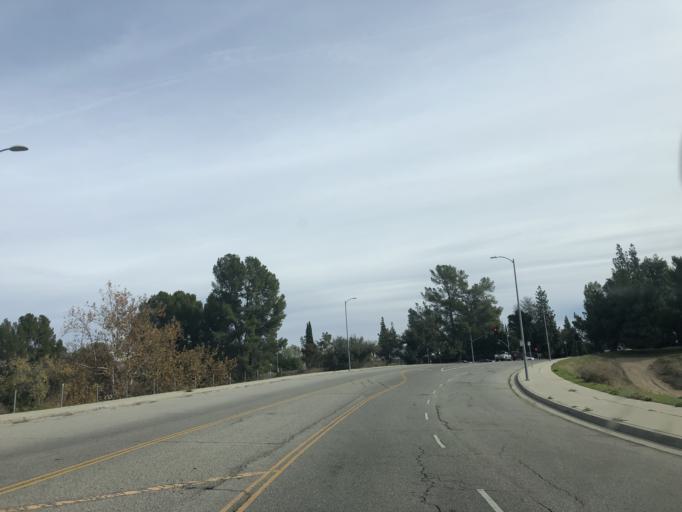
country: US
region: California
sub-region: Los Angeles County
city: Northridge
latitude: 34.2658
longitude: -118.5568
